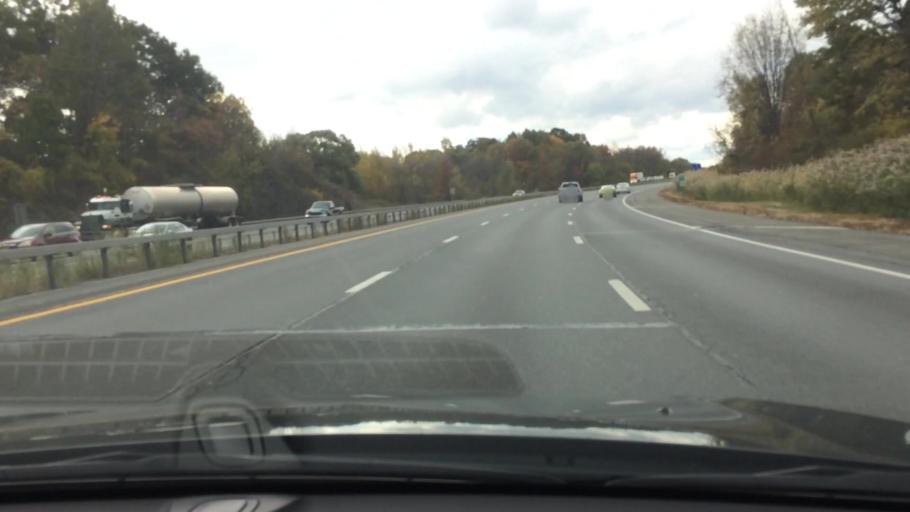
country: US
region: New York
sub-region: Albany County
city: Cohoes
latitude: 42.7866
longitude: -73.7581
